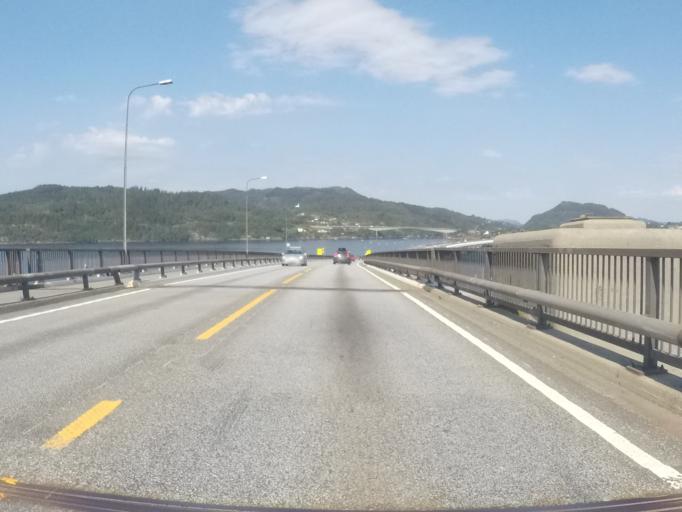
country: NO
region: Hordaland
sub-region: Lindas
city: Knarvik
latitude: 60.5210
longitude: 5.2708
